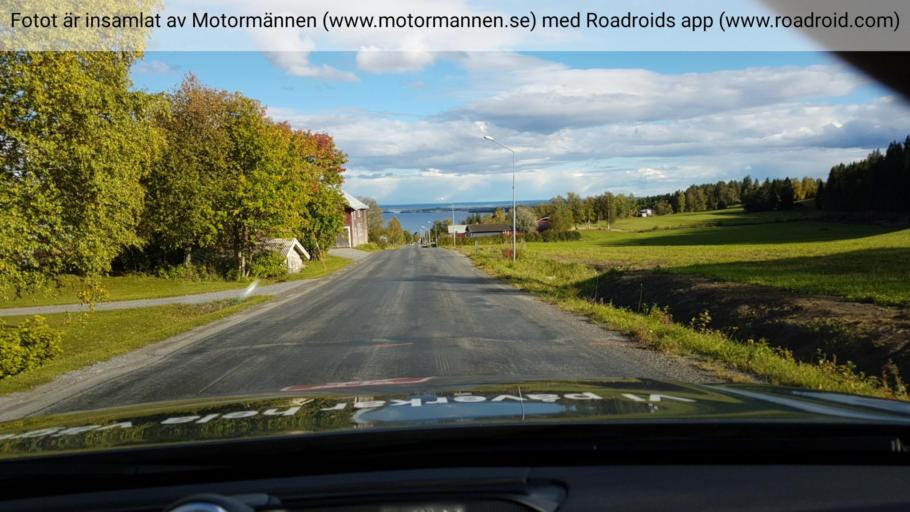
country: SE
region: Jaemtland
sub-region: Krokoms Kommun
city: Krokom
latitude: 63.1815
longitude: 14.0692
